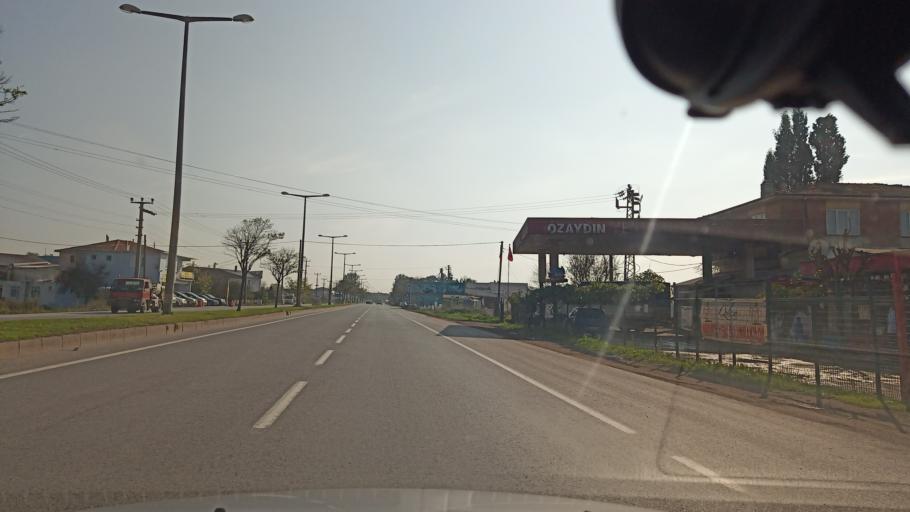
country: TR
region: Sakarya
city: Adapazari
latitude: 40.8170
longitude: 30.4007
